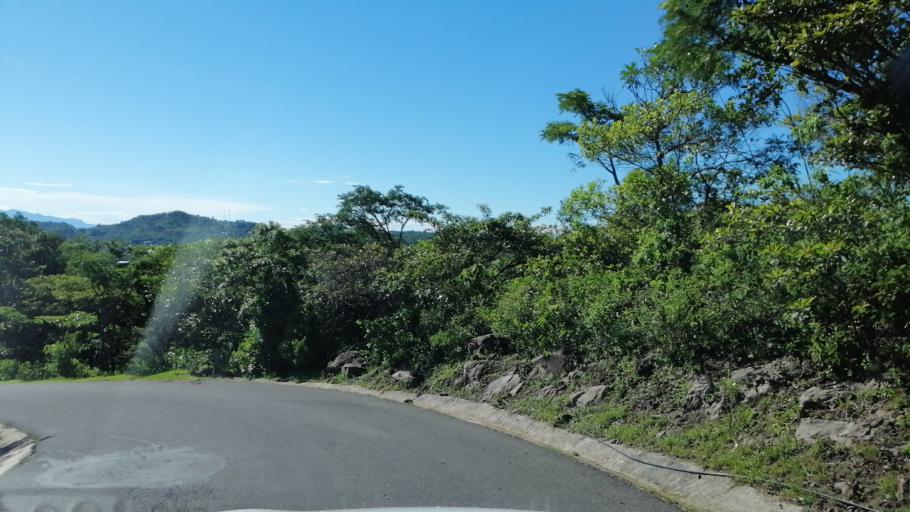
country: SV
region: Morazan
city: Corinto
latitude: 13.8103
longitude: -87.9884
